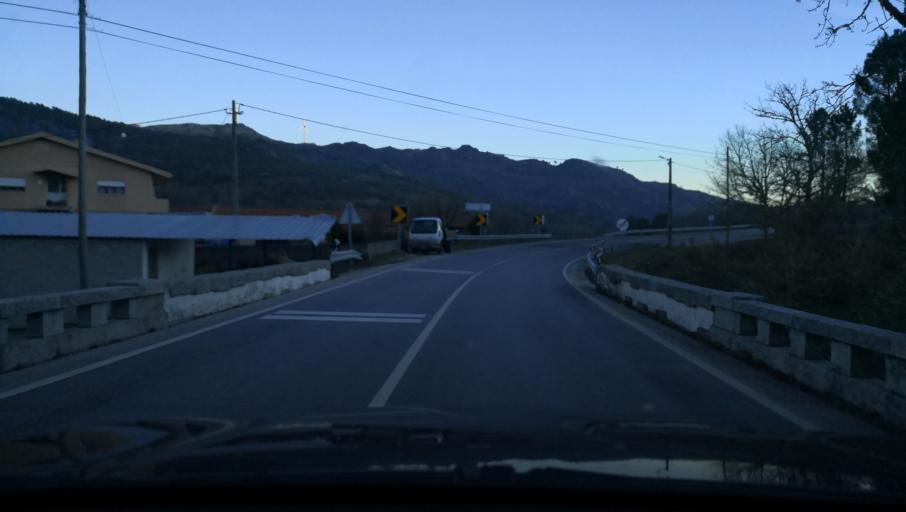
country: PT
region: Vila Real
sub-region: Vila Pouca de Aguiar
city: Vila Pouca de Aguiar
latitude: 41.4210
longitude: -7.6854
